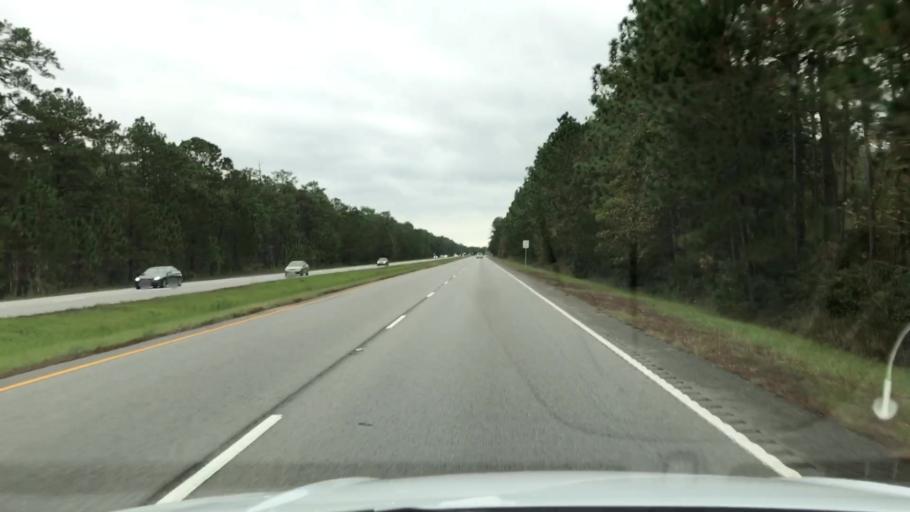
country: US
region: South Carolina
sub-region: Georgetown County
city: Georgetown
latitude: 33.4086
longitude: -79.1934
